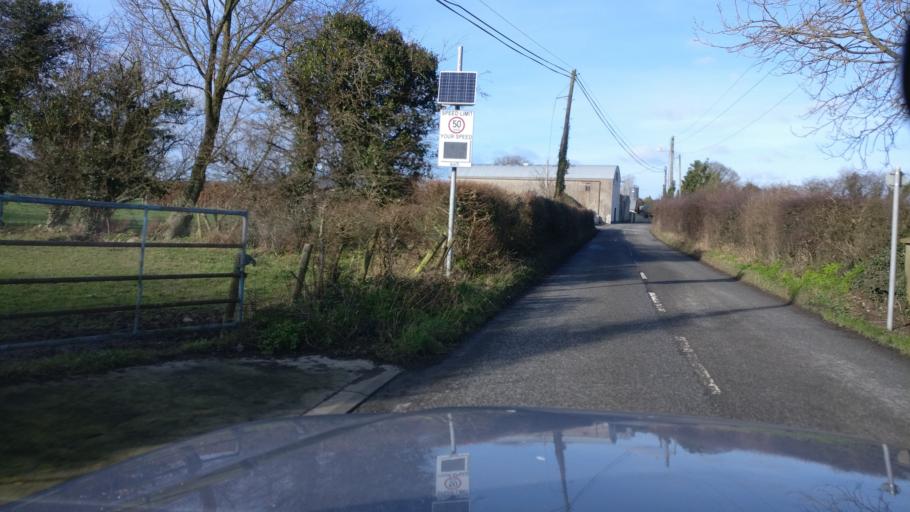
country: IE
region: Leinster
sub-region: Kilkenny
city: Castlecomer
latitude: 52.8630
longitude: -7.1644
